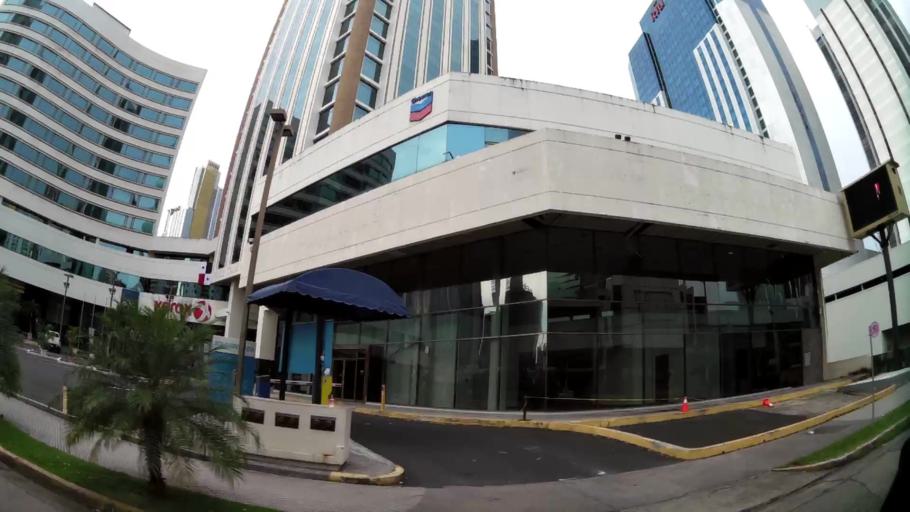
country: PA
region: Panama
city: Panama
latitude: 8.9808
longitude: -79.5199
